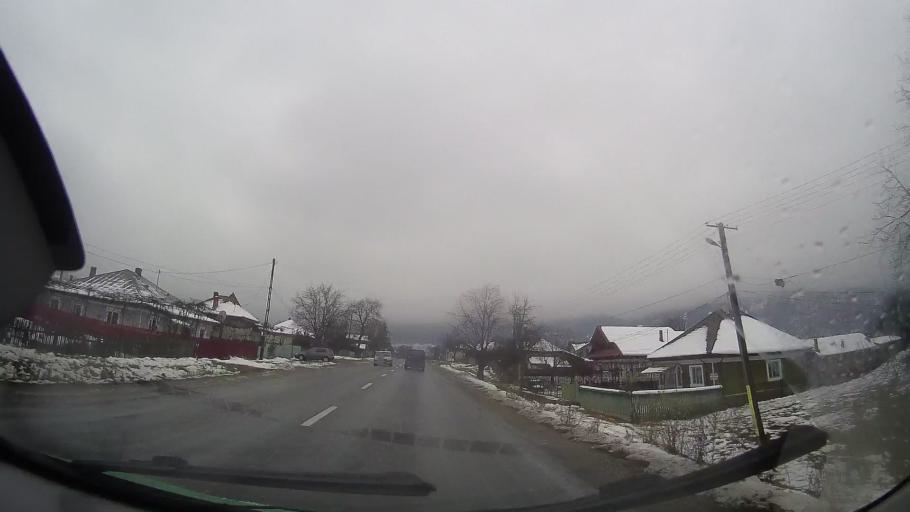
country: RO
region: Neamt
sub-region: Comuna Pangarati
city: Stejaru
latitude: 46.9141
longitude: 26.1843
